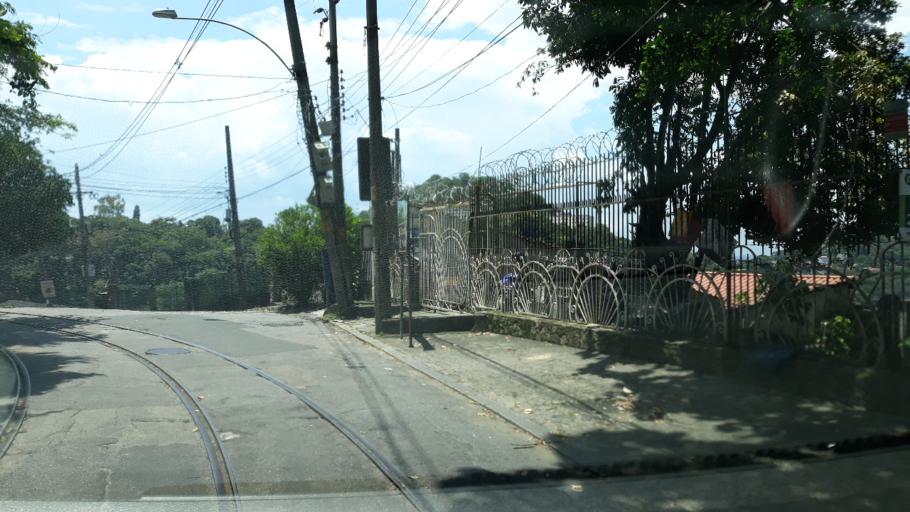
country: BR
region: Rio de Janeiro
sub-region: Rio De Janeiro
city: Rio de Janeiro
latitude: -22.9427
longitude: -43.2076
